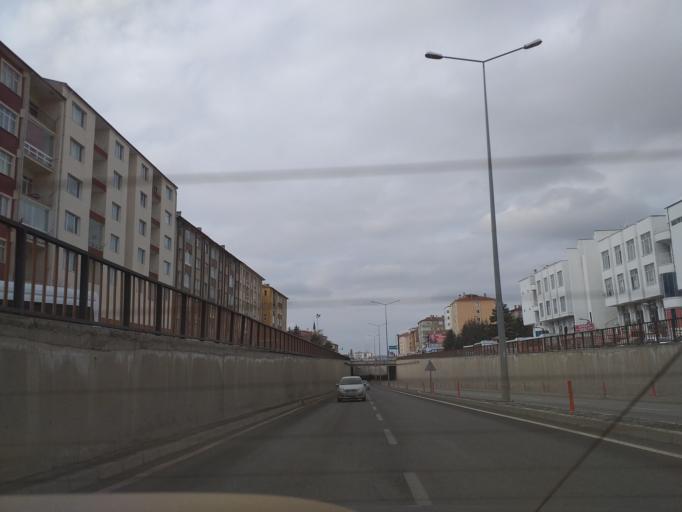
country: TR
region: Yozgat
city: Yozgat
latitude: 39.8216
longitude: 34.8117
